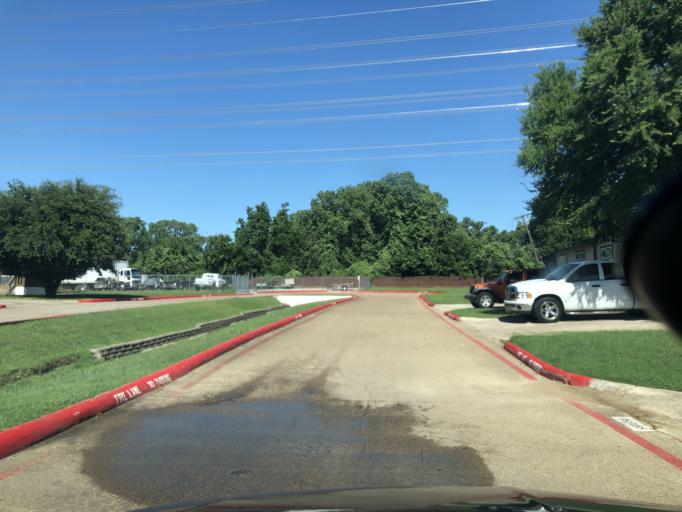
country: US
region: Texas
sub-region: Dallas County
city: Grand Prairie
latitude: 32.8013
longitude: -97.0260
